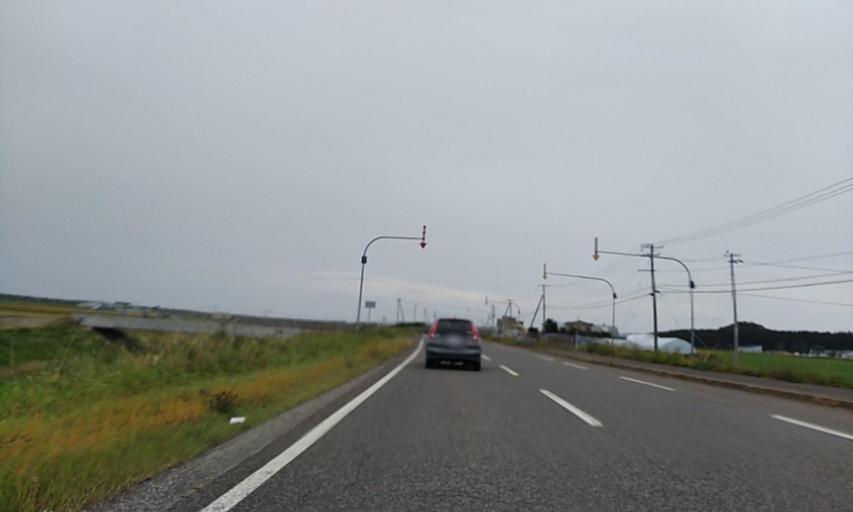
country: JP
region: Hokkaido
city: Bihoro
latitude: 43.9003
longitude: 144.1491
